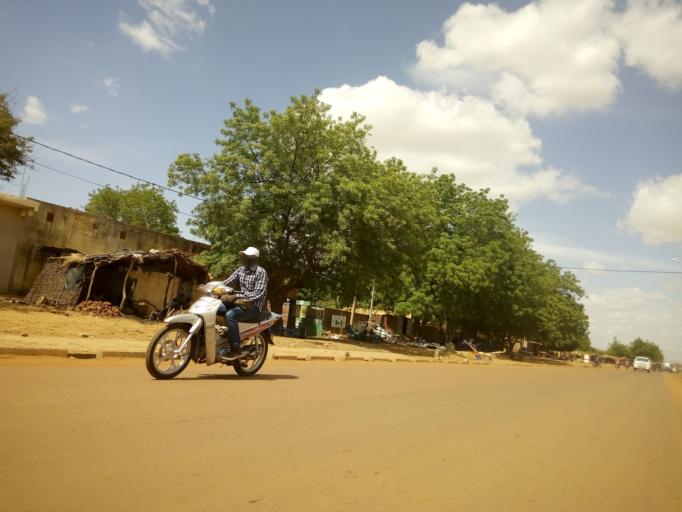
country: ML
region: Segou
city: Segou
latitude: 13.4422
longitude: -6.2431
